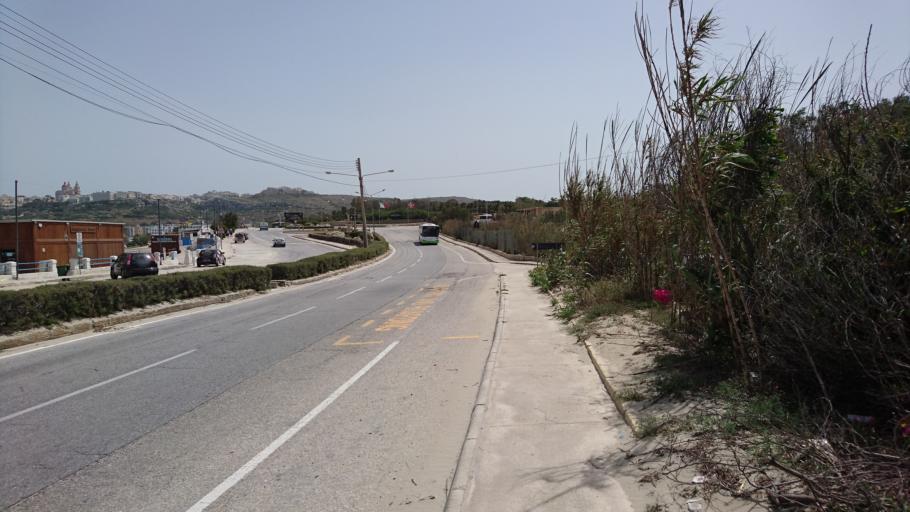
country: MT
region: Il-Mellieha
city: Mellieha
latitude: 35.9707
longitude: 14.3493
